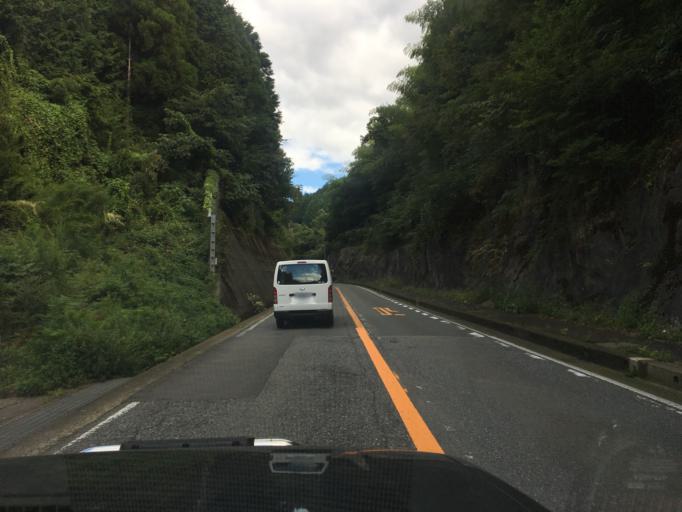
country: JP
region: Kyoto
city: Fukuchiyama
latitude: 35.3337
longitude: 134.9180
